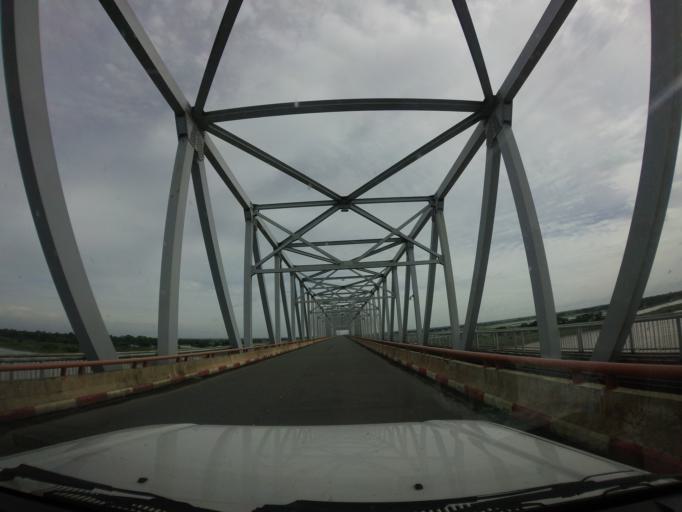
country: MM
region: Ayeyarwady
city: Nyaungdon
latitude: 17.0418
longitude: 95.5777
